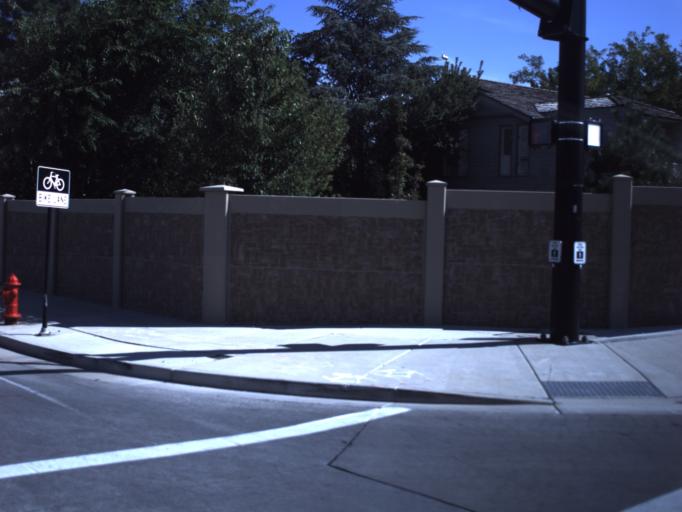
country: US
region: Utah
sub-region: Salt Lake County
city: South Jordan Heights
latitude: 40.5621
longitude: -111.9672
